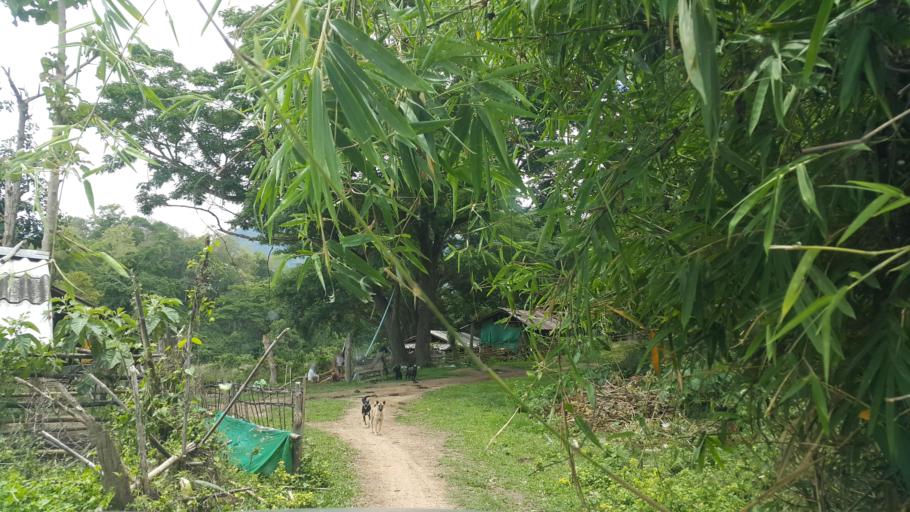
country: TH
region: Phayao
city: Phayao
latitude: 19.1776
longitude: 99.7672
